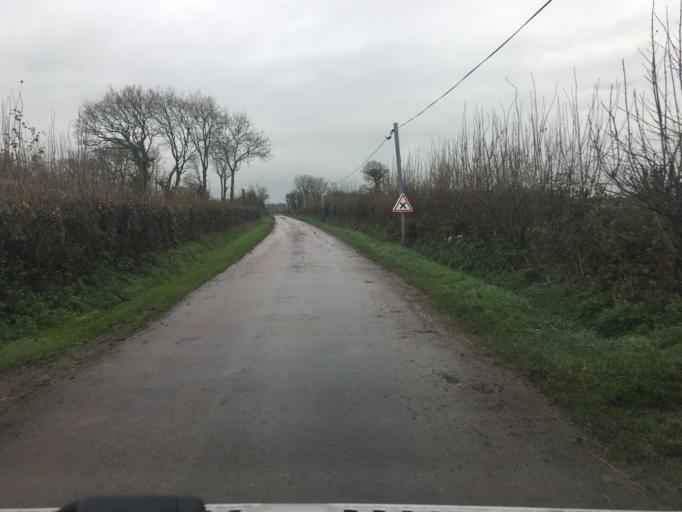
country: FR
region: Lower Normandy
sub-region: Departement de la Manche
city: Sainte-Mere-Eglise
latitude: 49.4292
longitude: -1.2627
